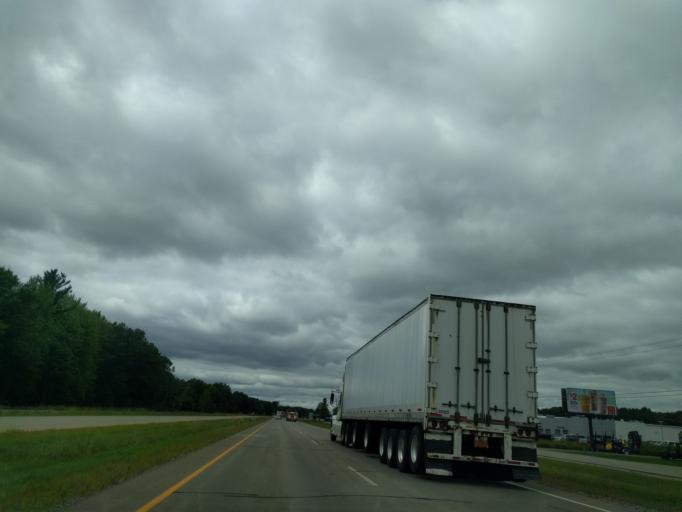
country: US
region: Wisconsin
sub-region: Marinette County
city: Marinette
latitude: 45.0714
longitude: -87.6804
